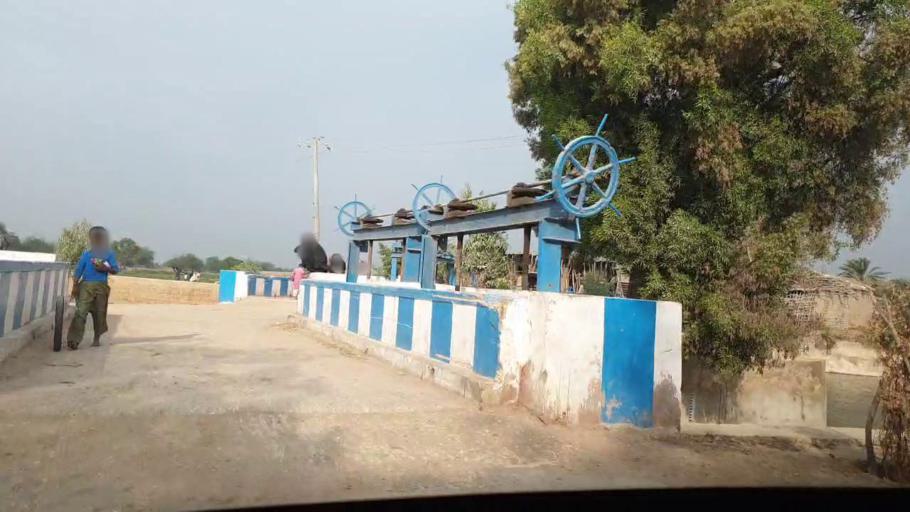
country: PK
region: Sindh
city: Chuhar Jamali
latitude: 24.3977
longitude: 67.9725
